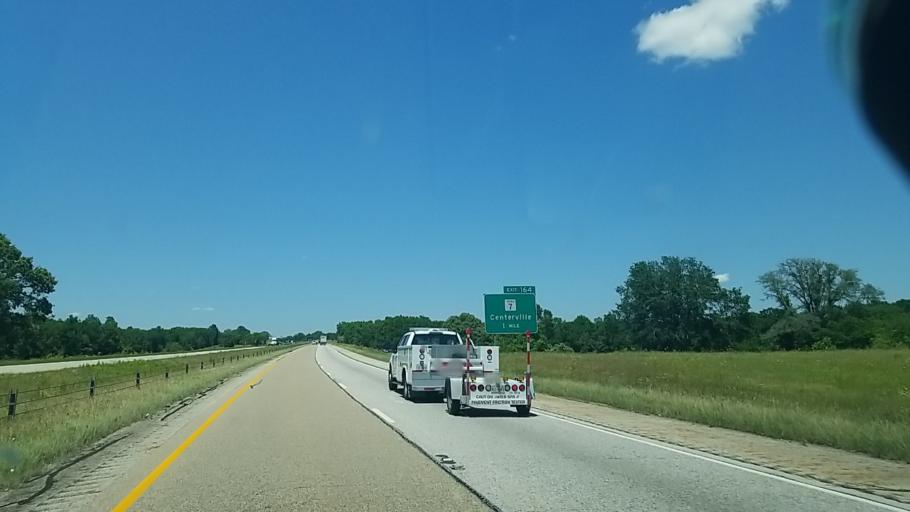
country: US
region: Texas
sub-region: Leon County
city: Centerville
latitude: 31.2401
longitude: -95.9921
